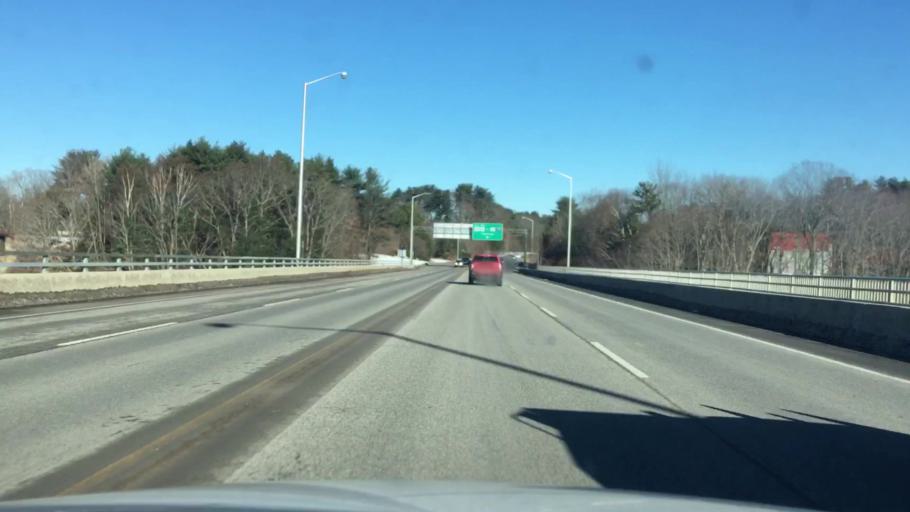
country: US
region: Maine
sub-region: Cumberland County
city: Brunswick
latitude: 43.9225
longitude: -69.9527
